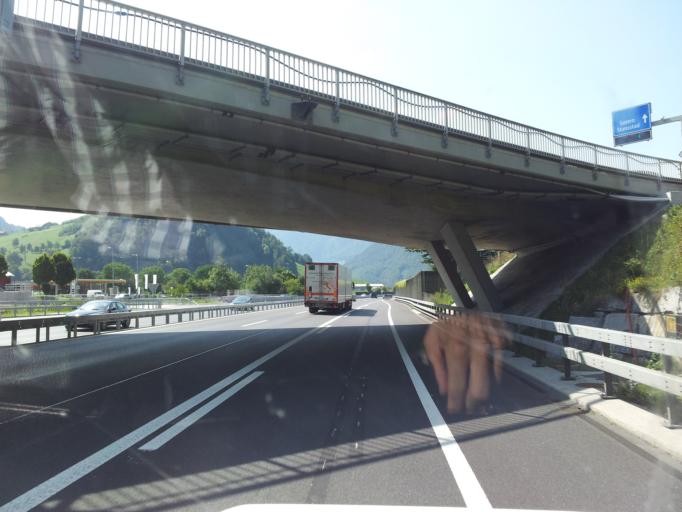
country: CH
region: Nidwalden
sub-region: Nidwalden
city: Stans
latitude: 46.9669
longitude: 8.3555
